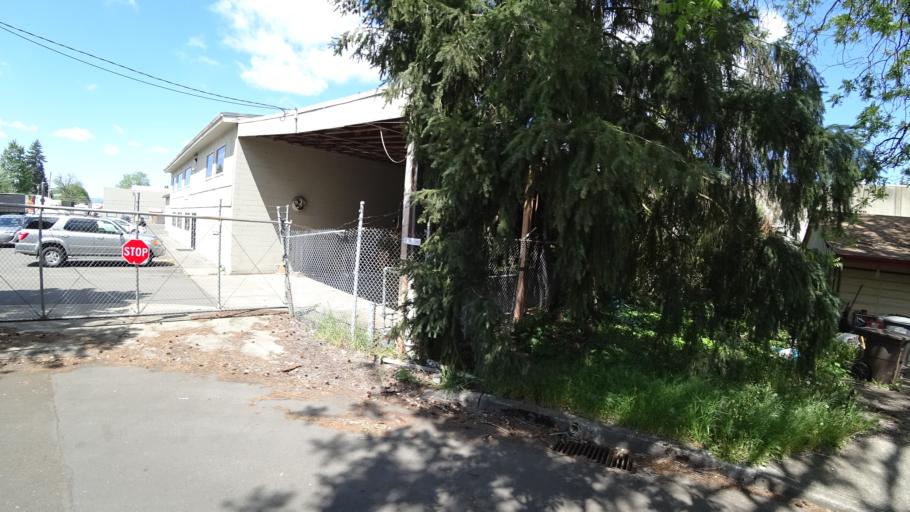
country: US
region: Oregon
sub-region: Washington County
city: Hillsboro
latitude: 45.5163
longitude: -122.9835
